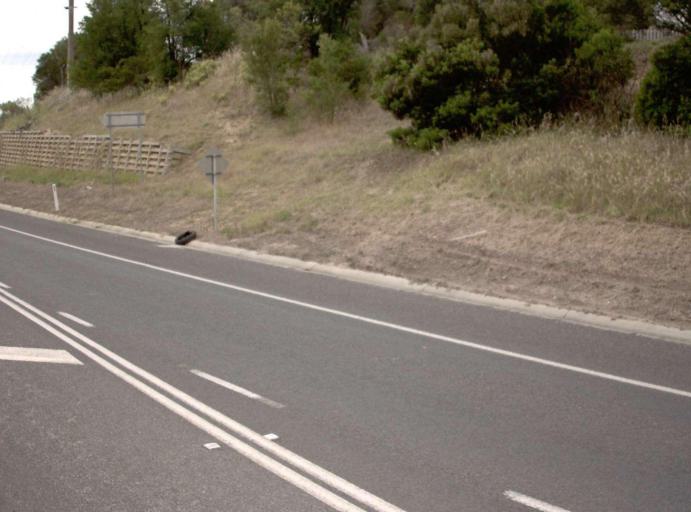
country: AU
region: Victoria
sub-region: Wellington
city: Sale
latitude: -38.1583
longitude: 147.0842
